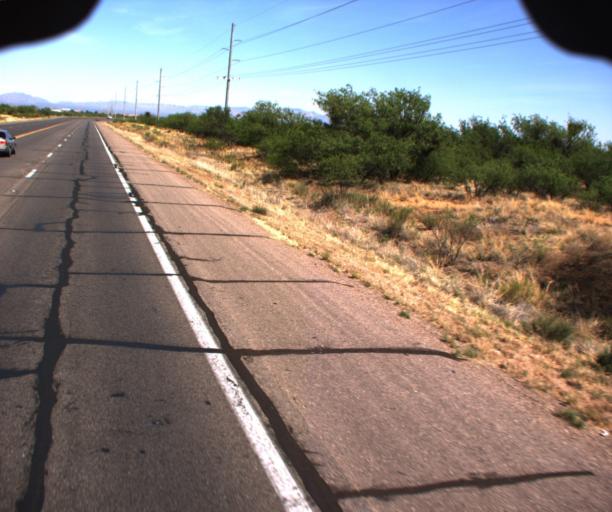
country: US
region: Arizona
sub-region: Cochise County
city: Sierra Vista
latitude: 31.5694
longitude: -110.2654
